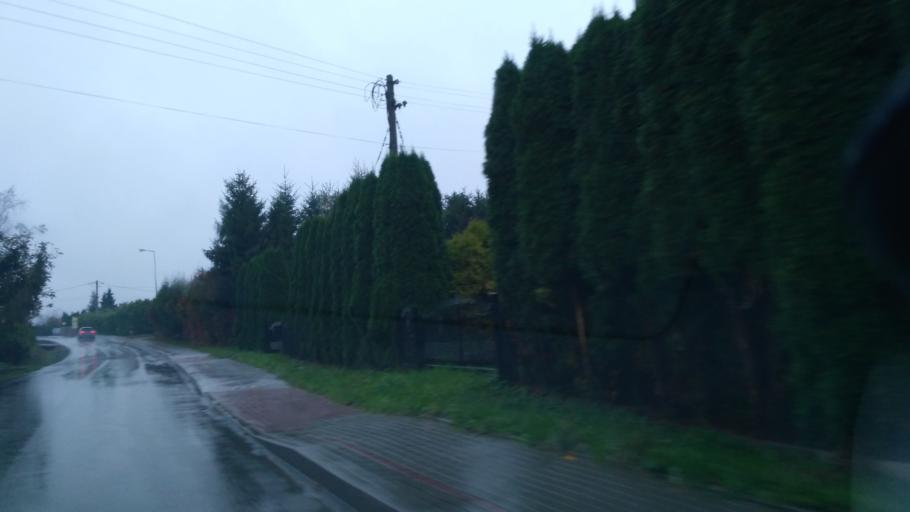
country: PL
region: Subcarpathian Voivodeship
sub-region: Powiat krosnienski
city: Korczyna
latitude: 49.7024
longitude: 21.8124
